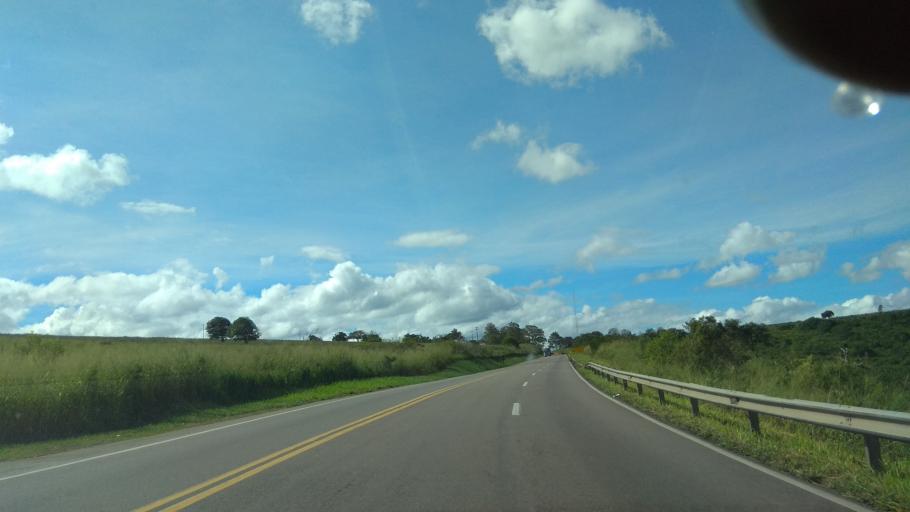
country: BR
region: Bahia
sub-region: Santa Ines
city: Santa Ines
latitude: -13.2037
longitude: -40.0151
